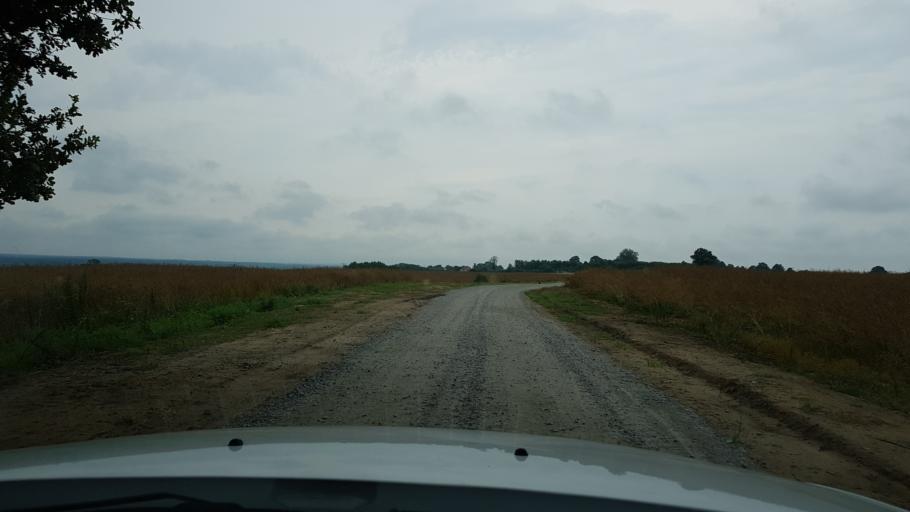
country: PL
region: West Pomeranian Voivodeship
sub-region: Powiat slawienski
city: Darlowo
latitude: 54.4632
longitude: 16.4994
